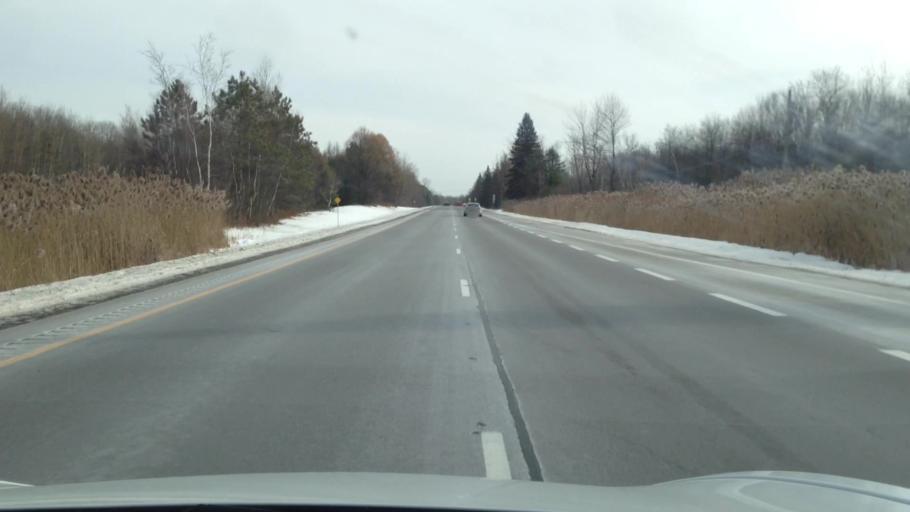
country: CA
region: Quebec
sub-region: Laurentides
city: Brownsburg-Chatham
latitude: 45.5525
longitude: -74.4475
